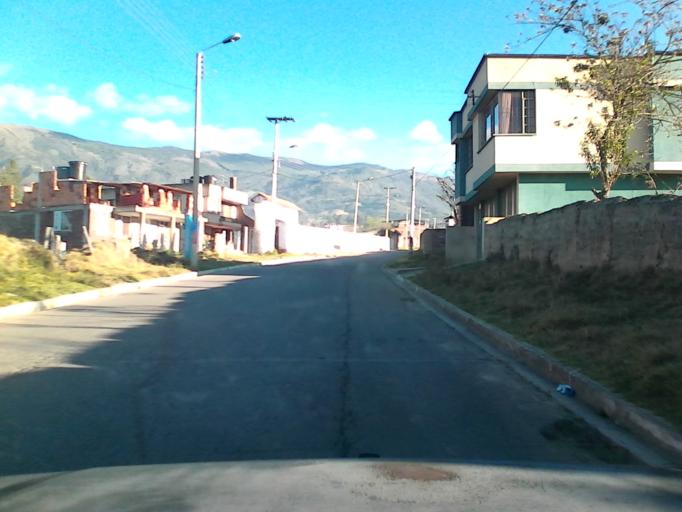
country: CO
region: Boyaca
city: Duitama
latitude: 5.8459
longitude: -73.0265
